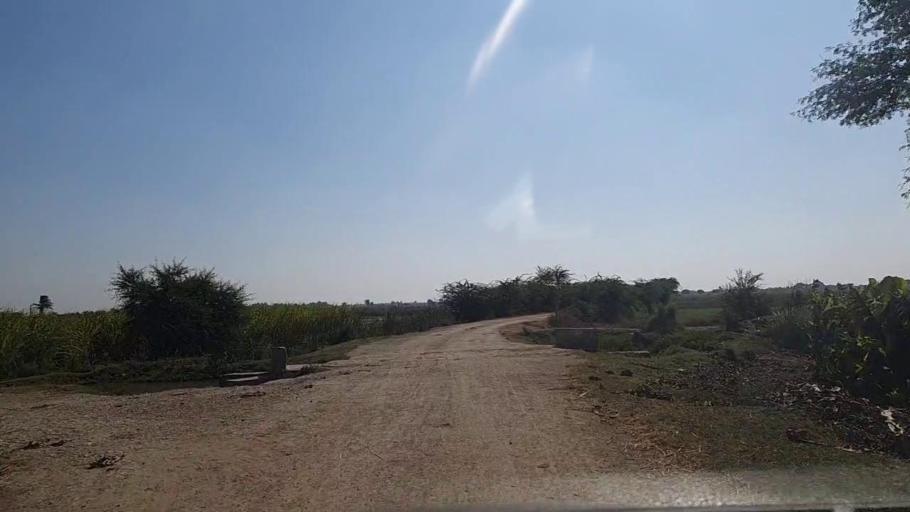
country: PK
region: Sindh
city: Mirpur Batoro
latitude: 24.6858
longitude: 68.1852
